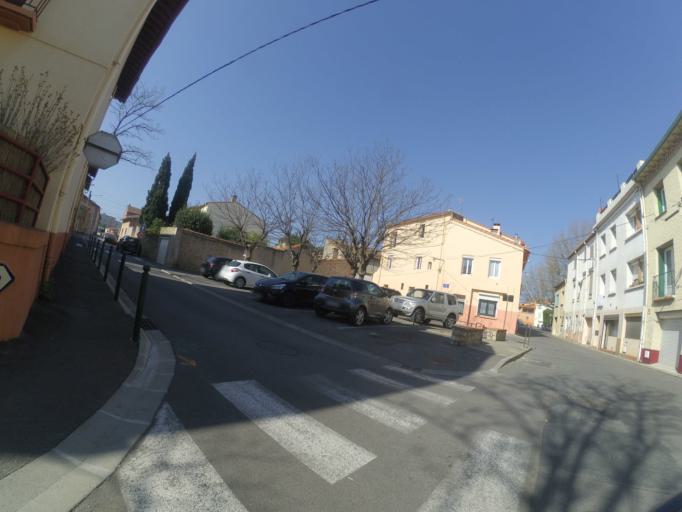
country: FR
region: Languedoc-Roussillon
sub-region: Departement des Pyrenees-Orientales
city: Thuir
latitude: 42.6322
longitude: 2.7544
